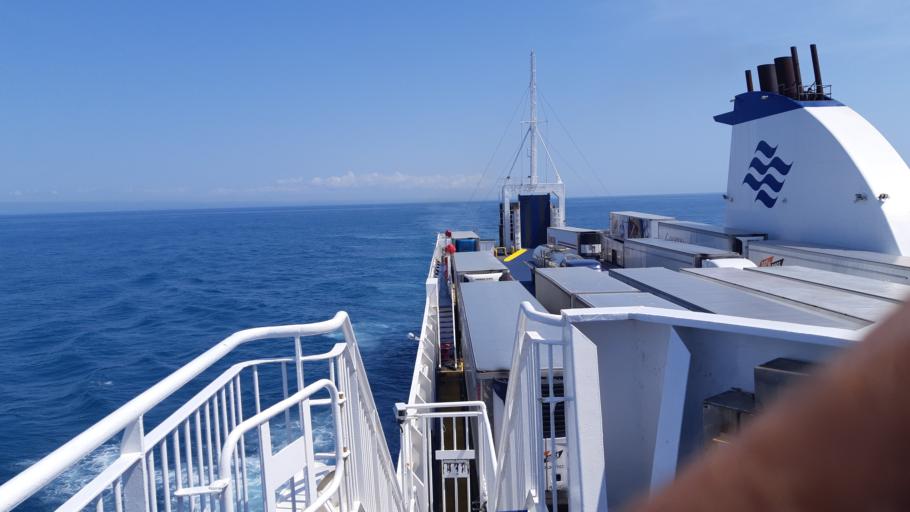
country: CA
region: Newfoundland and Labrador
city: Channel-Port aux Basques
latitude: 47.4271
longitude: -59.3802
